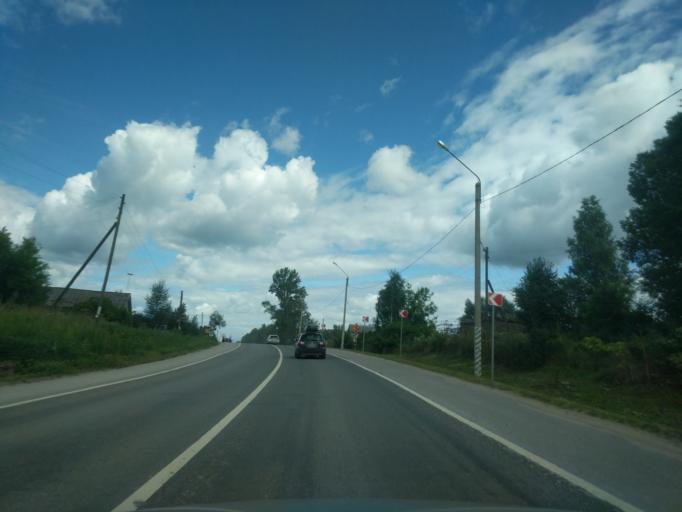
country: RU
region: Jaroslavl
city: Levashevo
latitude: 57.6556
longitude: 40.5624
